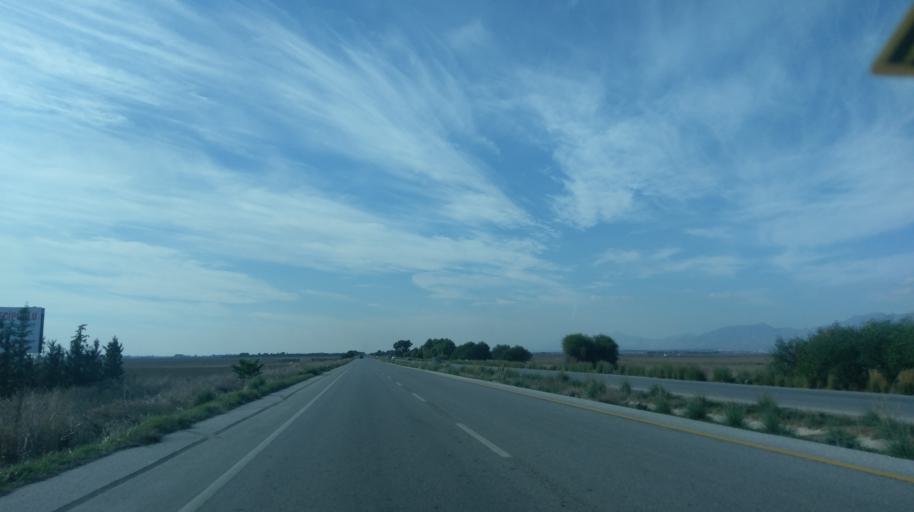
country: CY
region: Ammochostos
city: Lefkonoiko
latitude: 35.1841
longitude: 33.6818
